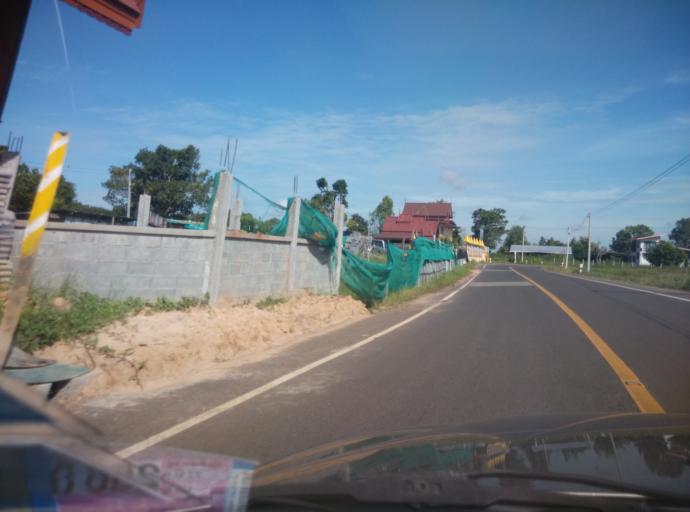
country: TH
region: Sisaket
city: Si Sa Ket
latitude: 15.1191
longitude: 104.2522
